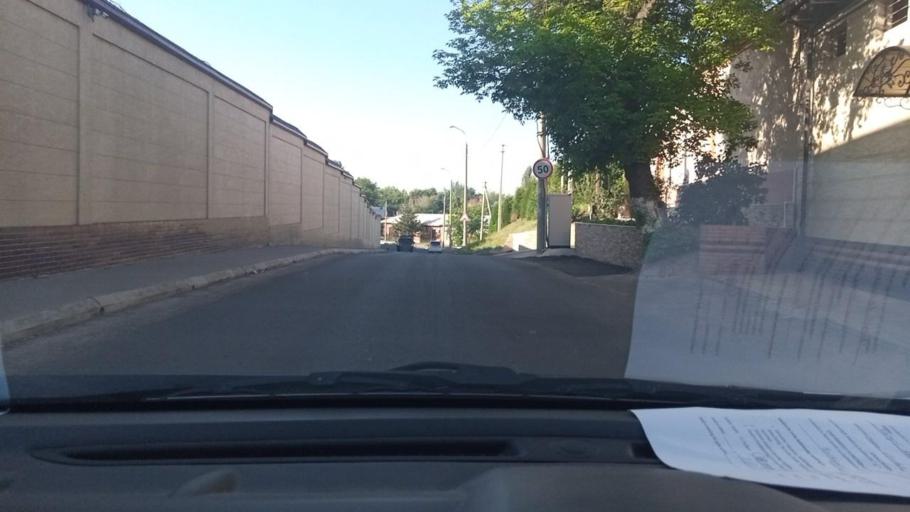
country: UZ
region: Toshkent
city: Salor
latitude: 41.3268
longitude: 69.3534
